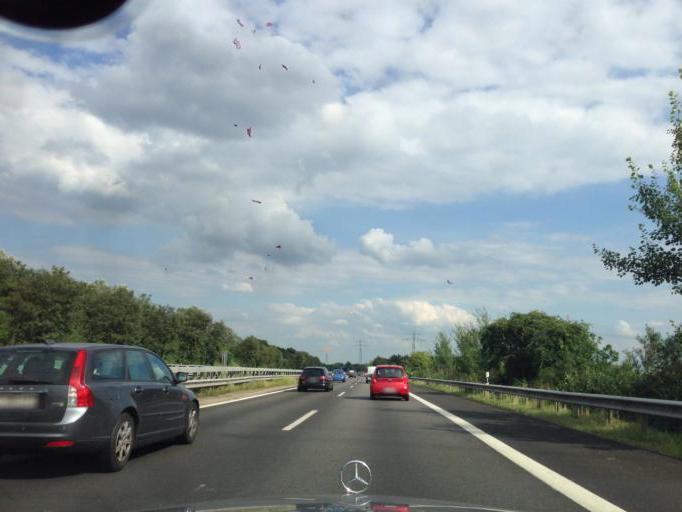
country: DE
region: Hamburg
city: Bergedorf
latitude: 53.4782
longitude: 10.1576
